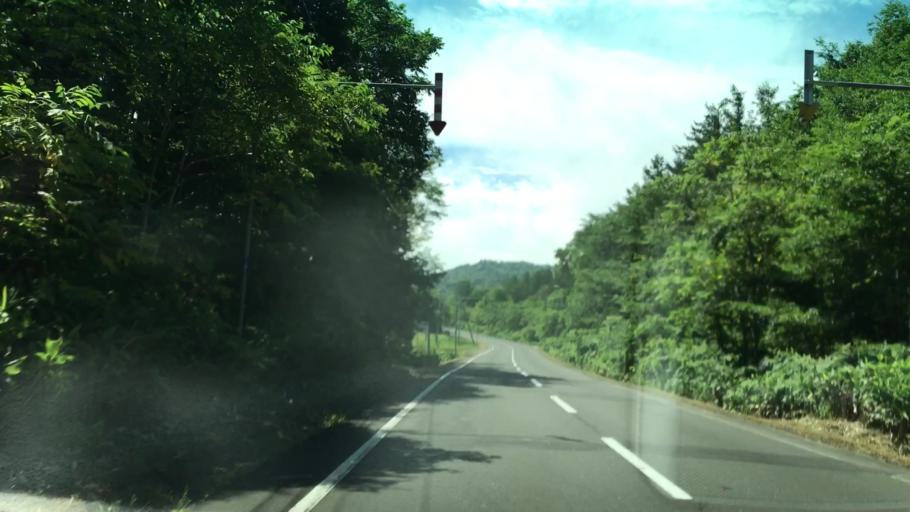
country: JP
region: Hokkaido
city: Shimo-furano
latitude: 42.9607
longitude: 142.4284
